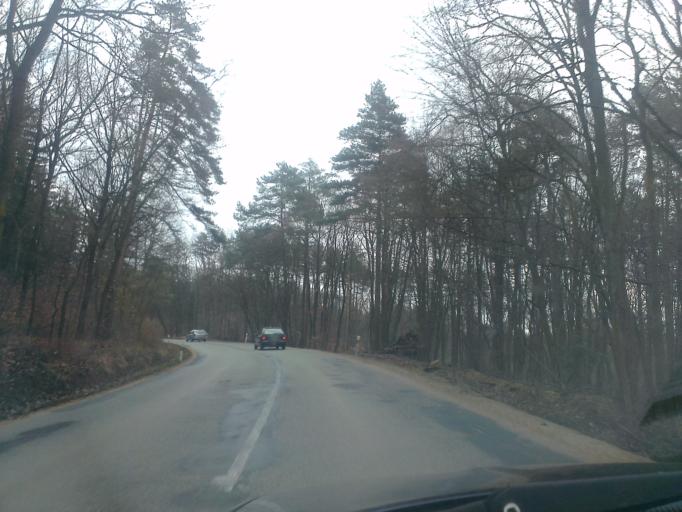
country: CZ
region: South Moravian
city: Bilovice nad Svitavou
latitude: 49.2437
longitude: 16.7158
